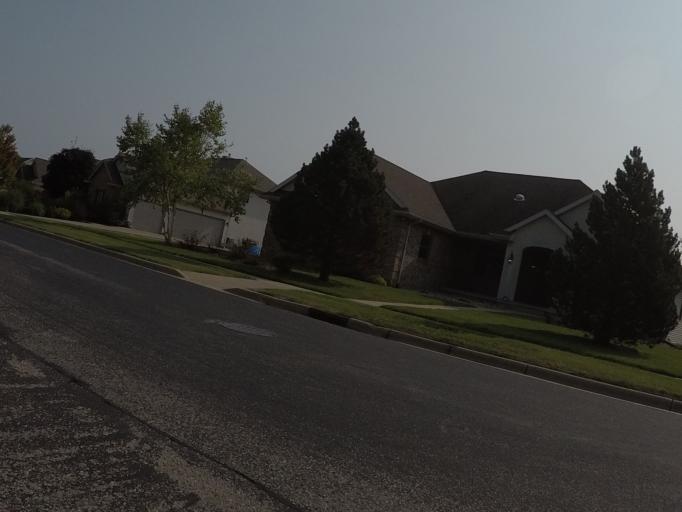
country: US
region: Wisconsin
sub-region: Dane County
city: Verona
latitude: 43.0326
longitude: -89.5367
